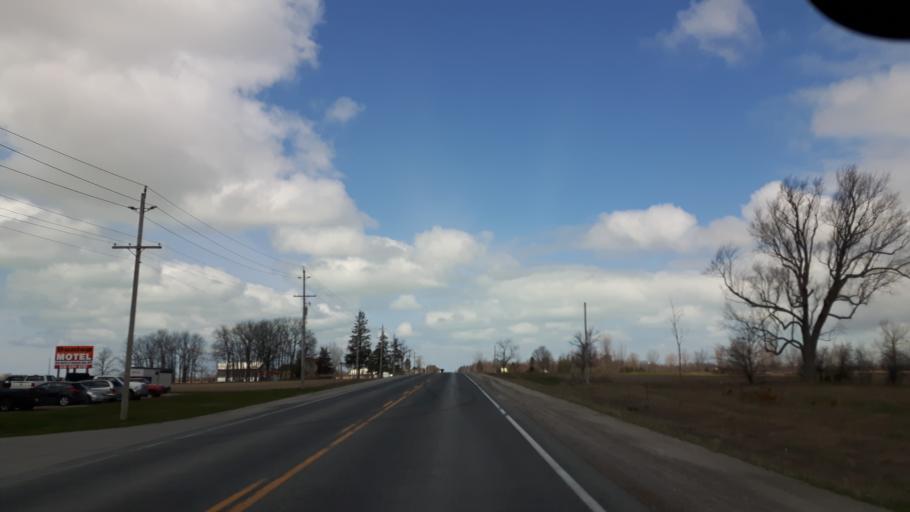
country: CA
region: Ontario
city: Goderich
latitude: 43.7185
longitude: -81.6720
